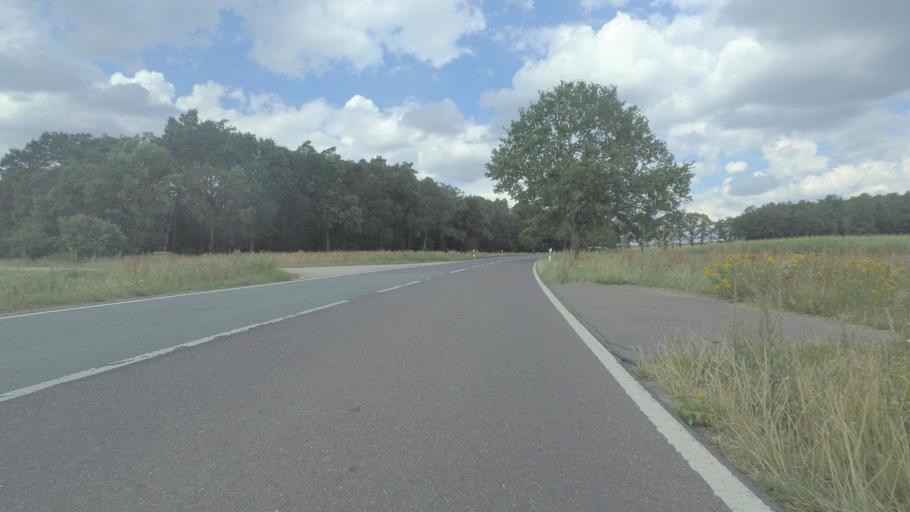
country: DE
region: Brandenburg
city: Wittstock
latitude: 53.2218
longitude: 12.4359
